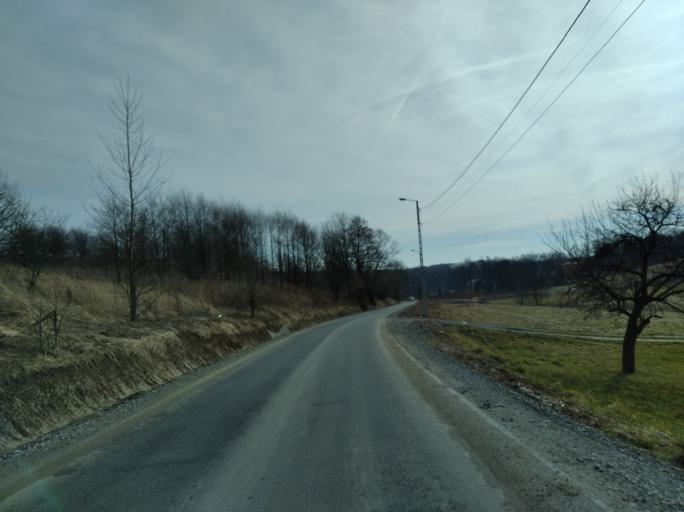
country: PL
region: Subcarpathian Voivodeship
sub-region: Powiat brzozowski
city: Jasienica Rosielna
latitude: 49.7624
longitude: 21.9452
